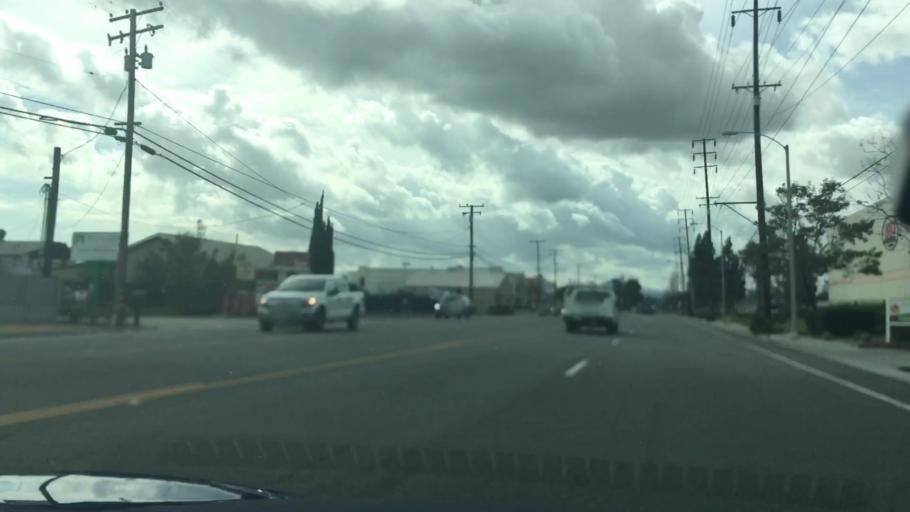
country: US
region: California
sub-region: Riverside County
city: Highgrove
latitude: 34.0166
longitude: -117.3629
